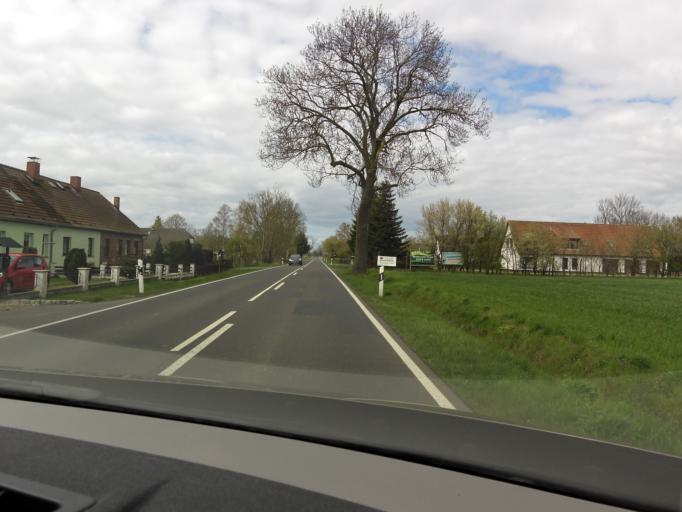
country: DE
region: Mecklenburg-Vorpommern
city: Gingst
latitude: 54.4363
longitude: 13.2701
